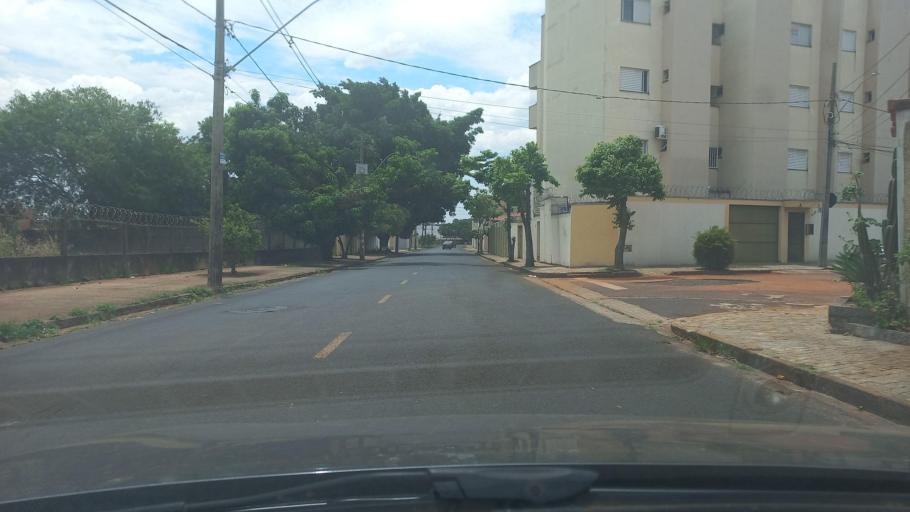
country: BR
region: Minas Gerais
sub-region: Uberaba
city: Uberaba
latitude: -19.7540
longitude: -47.9689
